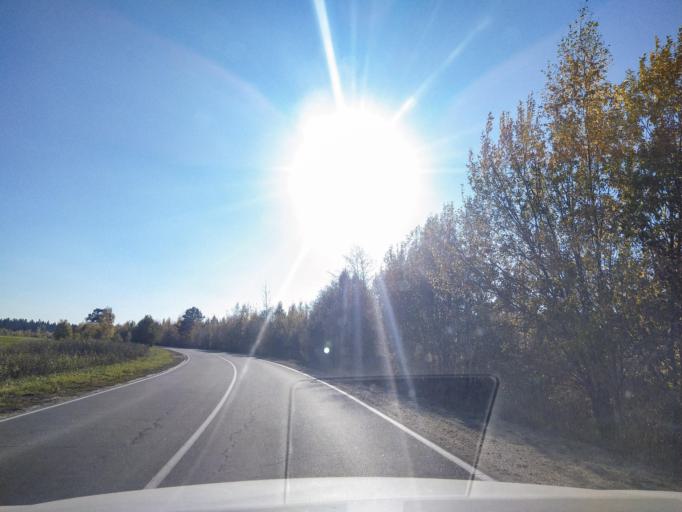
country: RU
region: Leningrad
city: Siverskiy
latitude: 59.3174
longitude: 30.0347
